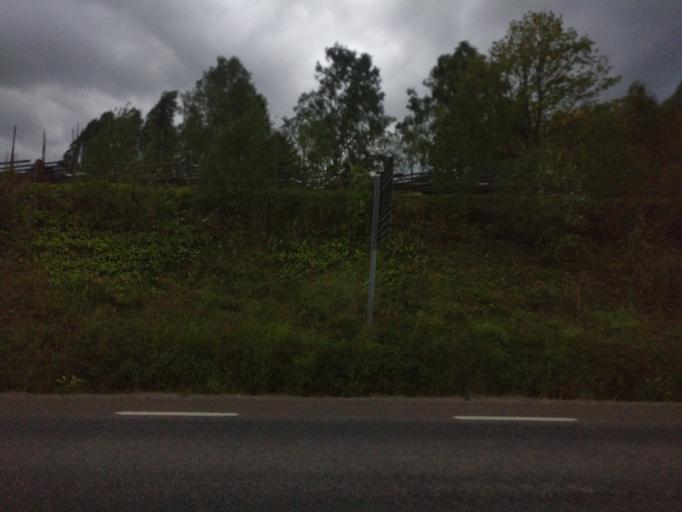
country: SE
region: Vaermland
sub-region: Torsby Kommun
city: Torsby
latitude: 60.6132
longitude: 13.0446
